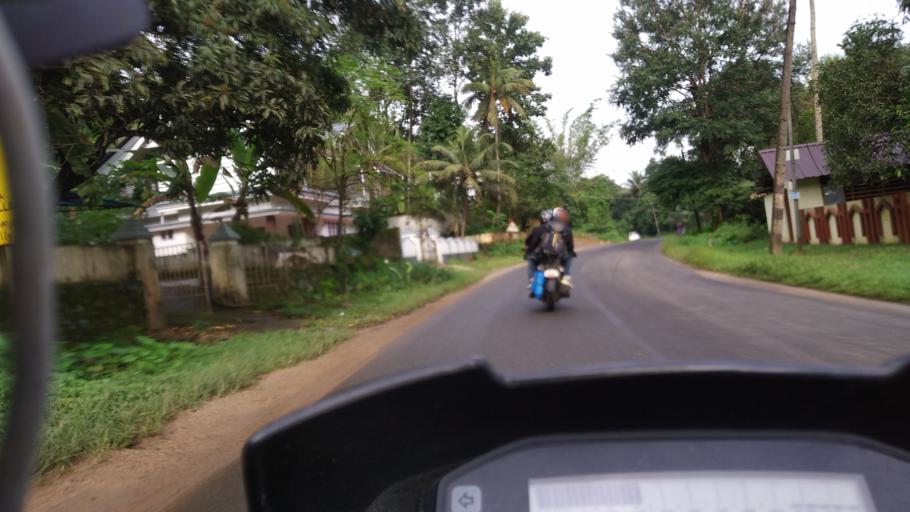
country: IN
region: Kerala
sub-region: Ernakulam
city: Kotamangalam
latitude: 10.0502
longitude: 76.7252
